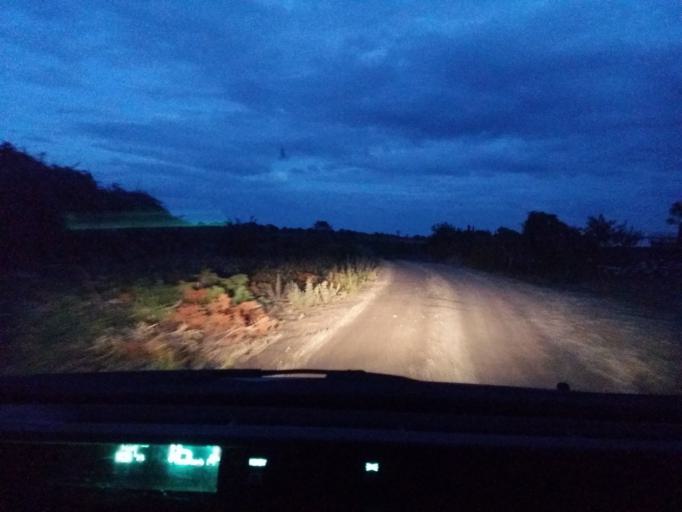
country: SE
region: Kalmar
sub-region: Borgholms Kommun
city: Borgholm
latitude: 57.1293
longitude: 16.9019
